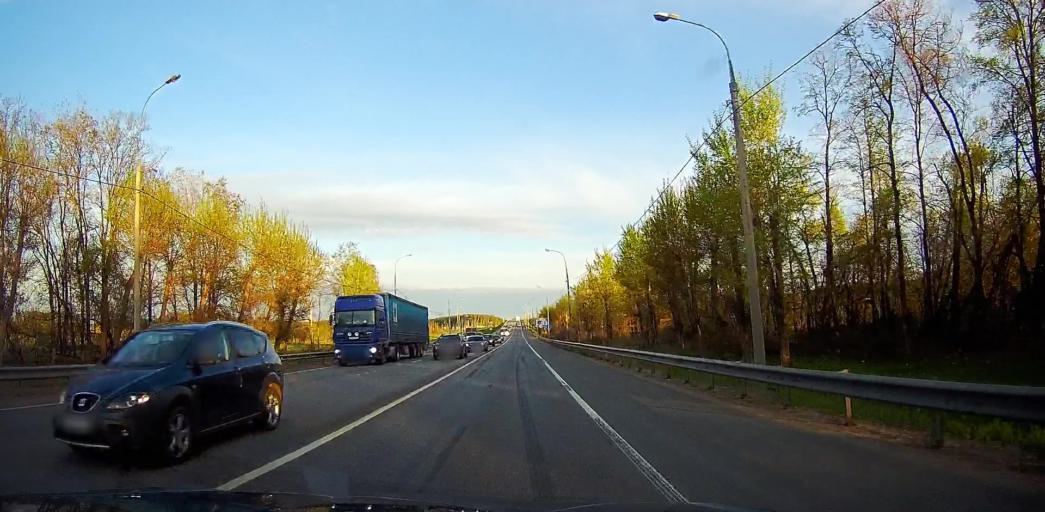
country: RU
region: Moskovskaya
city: Troitskoye
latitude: 55.2407
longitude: 38.5390
